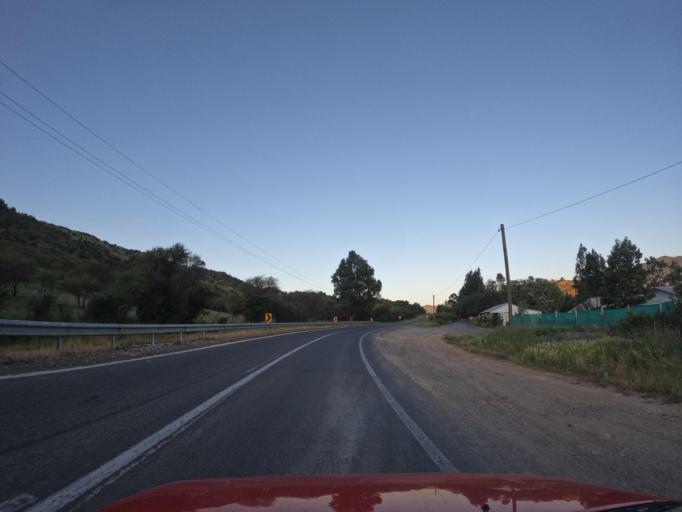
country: CL
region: Maule
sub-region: Provincia de Talca
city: Talca
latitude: -35.0796
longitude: -71.6353
